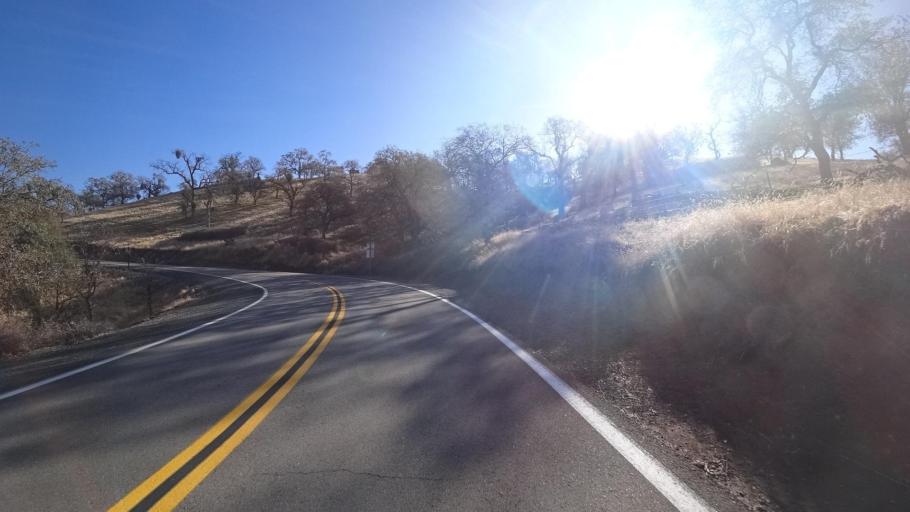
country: US
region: California
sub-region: Kern County
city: Alta Sierra
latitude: 35.7200
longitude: -118.7990
